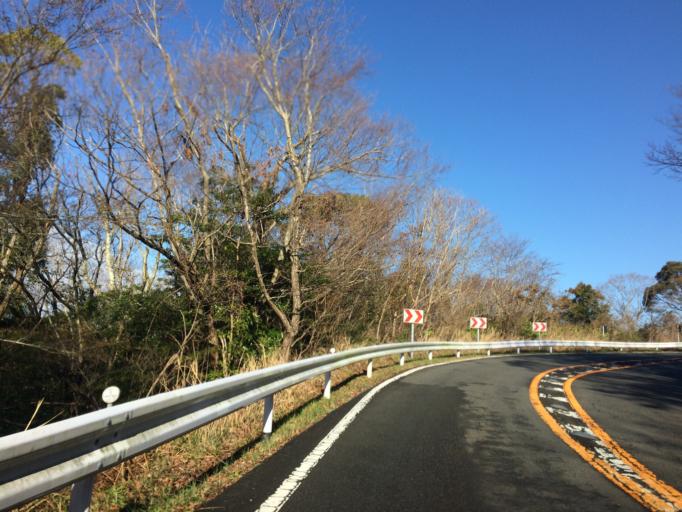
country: JP
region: Shizuoka
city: Shizuoka-shi
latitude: 34.9669
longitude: 138.4527
